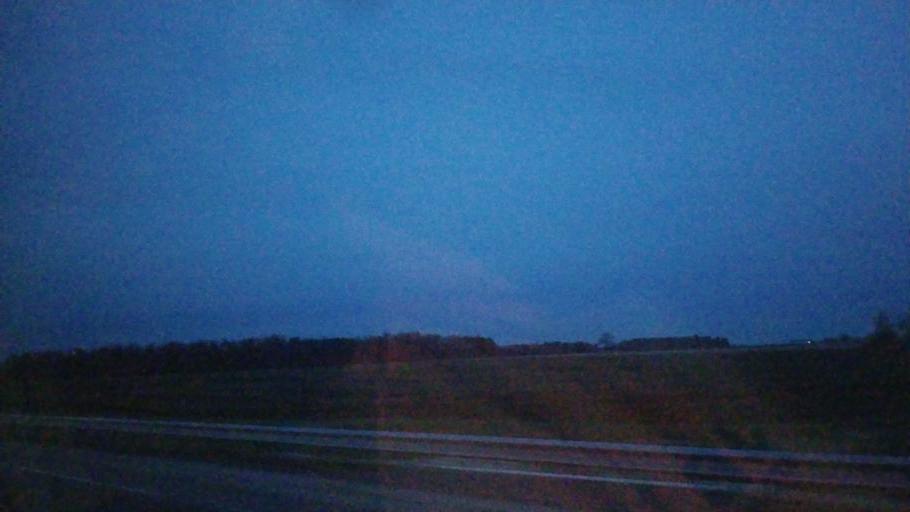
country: US
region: Indiana
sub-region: Adams County
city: Berne
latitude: 40.6737
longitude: -84.9557
